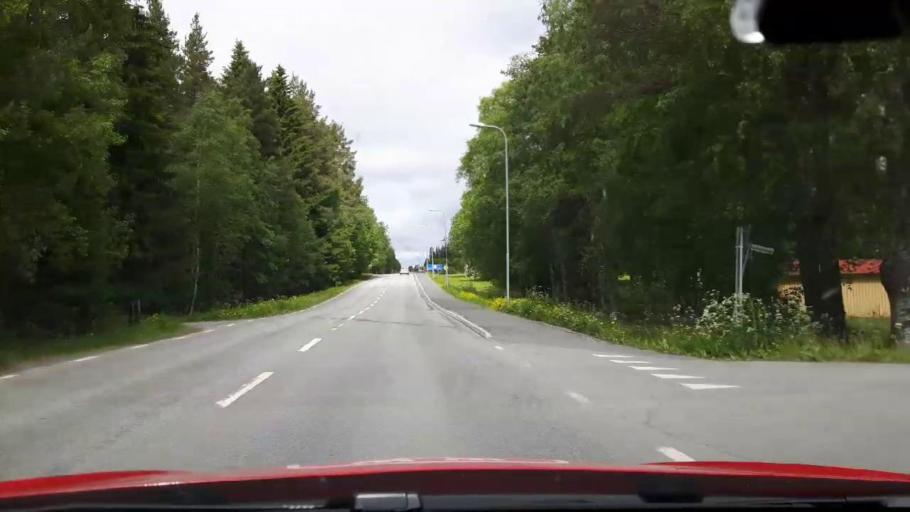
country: SE
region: Jaemtland
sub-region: Krokoms Kommun
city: Krokom
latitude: 63.3323
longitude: 14.4460
